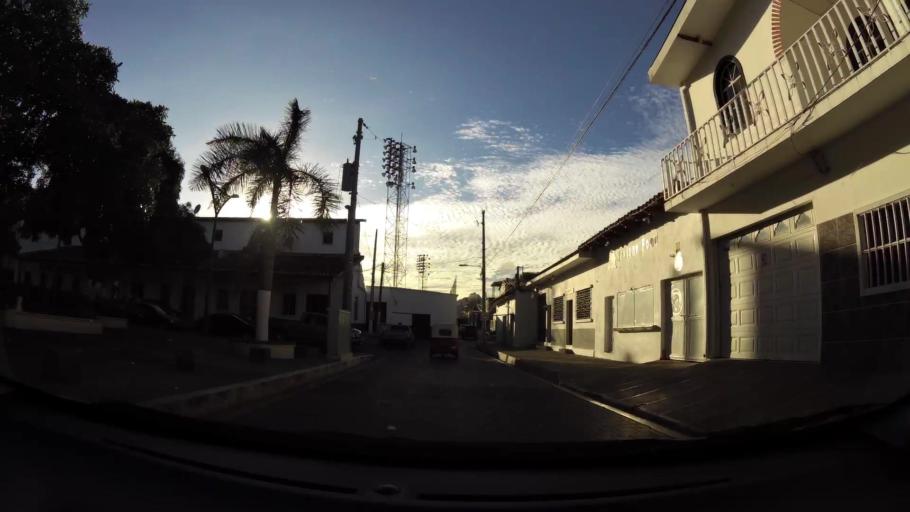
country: SV
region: Santa Ana
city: Metapan
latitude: 14.3326
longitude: -89.4482
